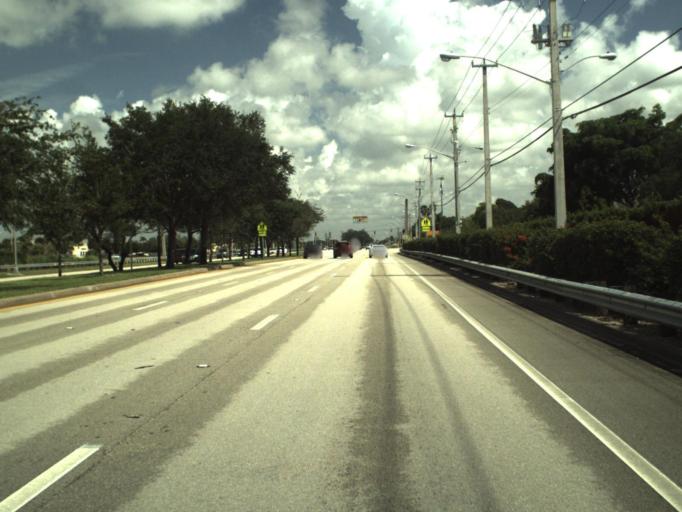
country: US
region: Florida
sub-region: Broward County
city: Sunshine Ranches
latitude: 26.0192
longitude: -80.3121
